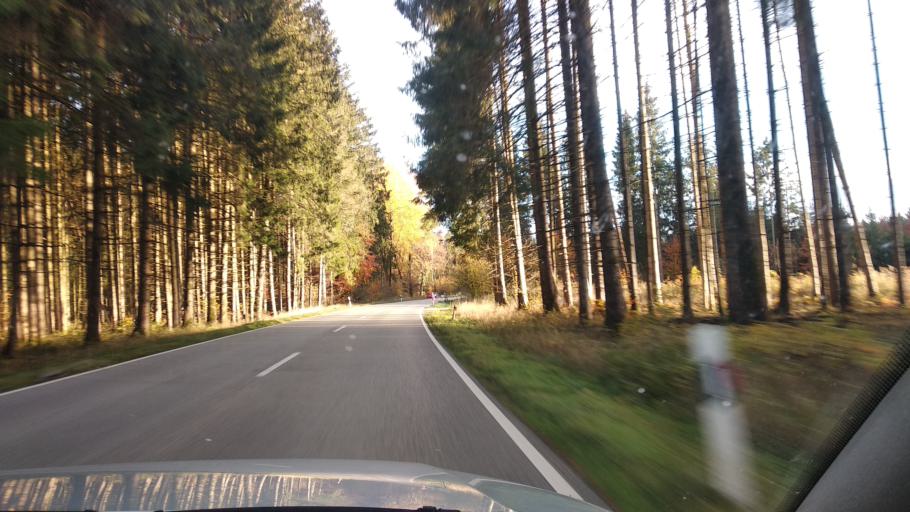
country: DE
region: Bavaria
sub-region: Upper Bavaria
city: Zorneding
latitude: 48.0684
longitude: 11.8402
